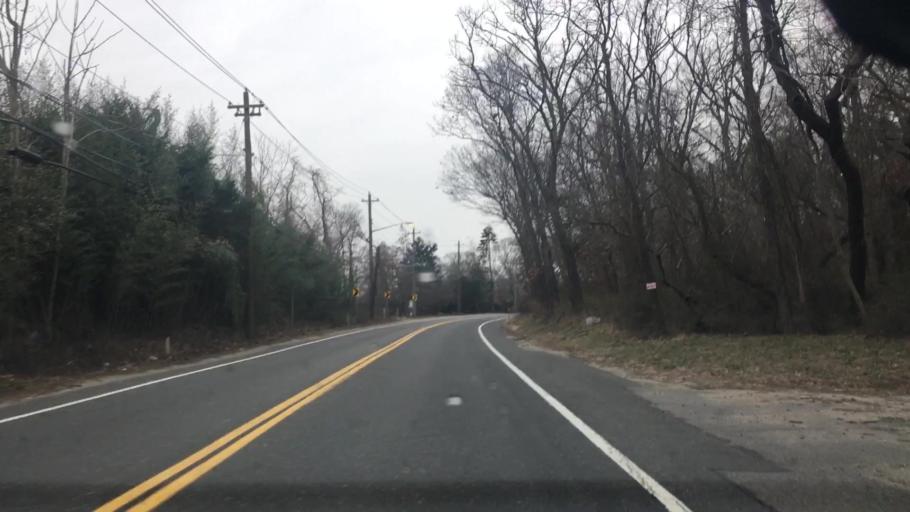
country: US
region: New York
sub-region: Suffolk County
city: Yaphank
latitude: 40.8481
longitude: -72.9359
